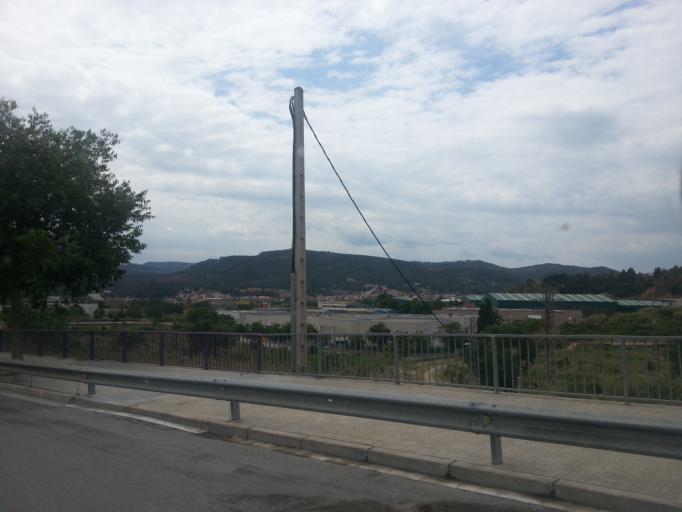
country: ES
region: Catalonia
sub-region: Provincia de Barcelona
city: Molins de Rei
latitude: 41.4208
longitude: 2.0174
